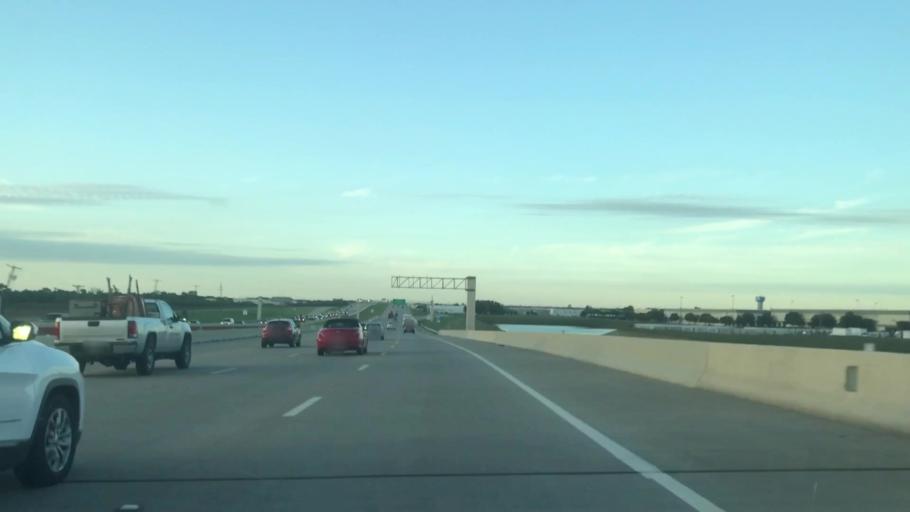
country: US
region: Texas
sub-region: Dallas County
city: Farmers Branch
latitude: 32.9275
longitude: -96.9306
